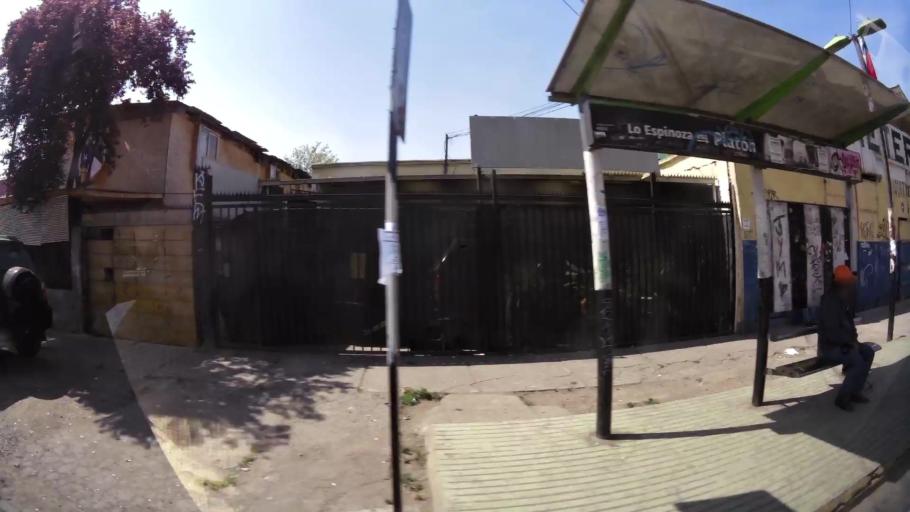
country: CL
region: Santiago Metropolitan
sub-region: Provincia de Santiago
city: Lo Prado
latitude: -33.4117
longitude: -70.7063
